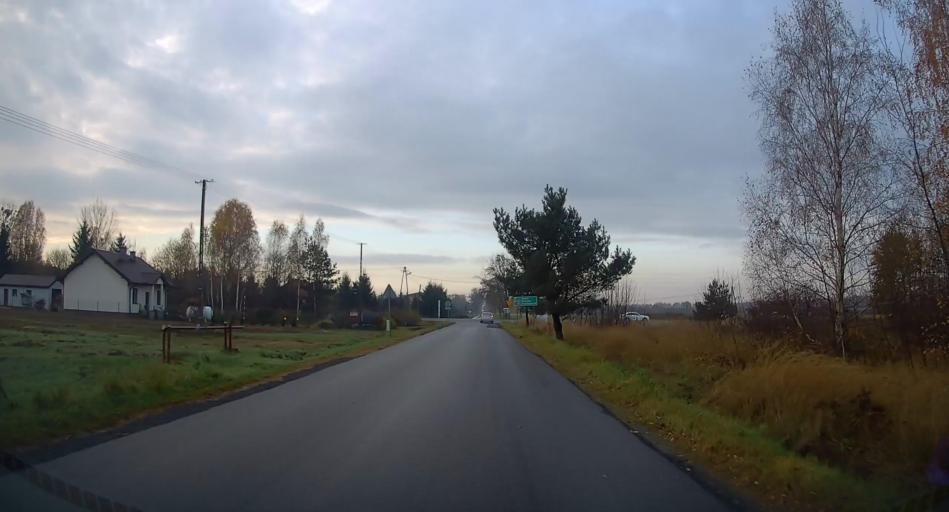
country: PL
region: Masovian Voivodeship
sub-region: Powiat zyrardowski
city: Puszcza Marianska
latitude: 51.9293
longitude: 20.3606
